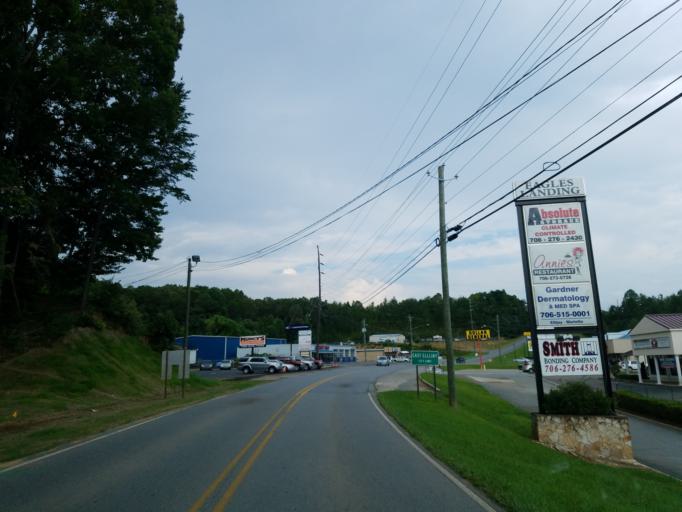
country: US
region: Georgia
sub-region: Gilmer County
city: Ellijay
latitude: 34.6801
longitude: -84.4861
